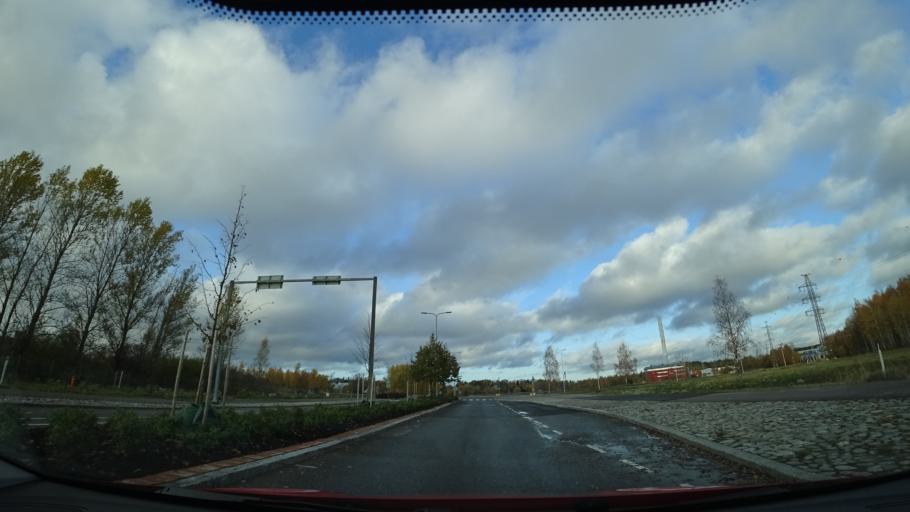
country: FI
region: Uusimaa
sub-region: Helsinki
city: Vantaa
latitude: 60.2865
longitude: 25.0583
